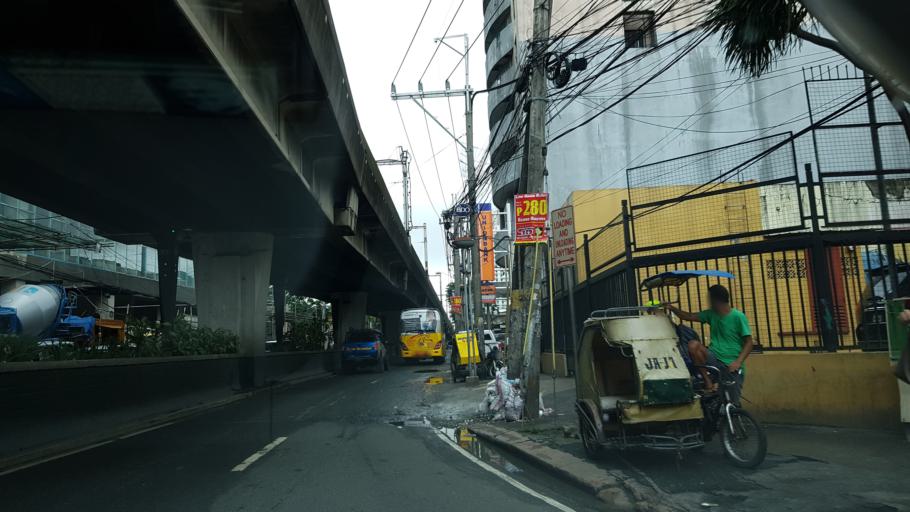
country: PH
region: Metro Manila
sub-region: City of Manila
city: Port Area
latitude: 14.5627
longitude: 120.9953
